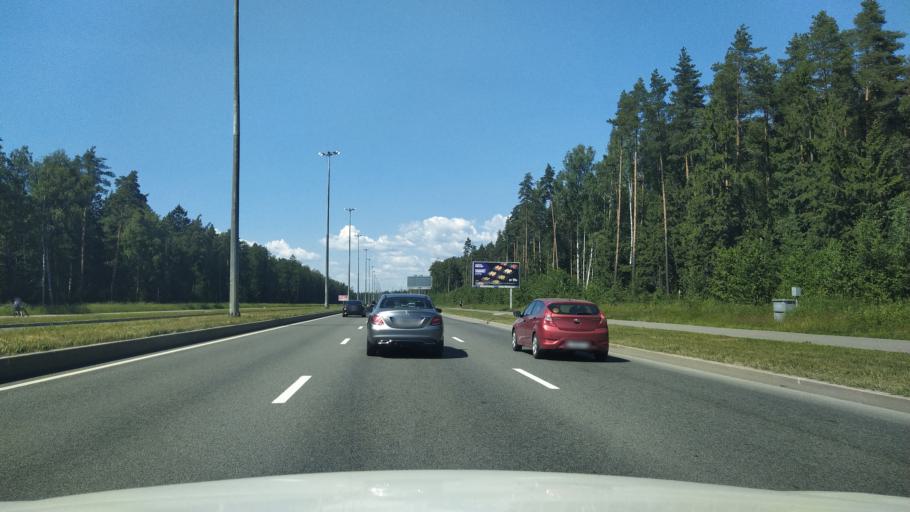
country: RU
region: Leningrad
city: Untolovo
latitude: 60.0547
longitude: 30.2250
